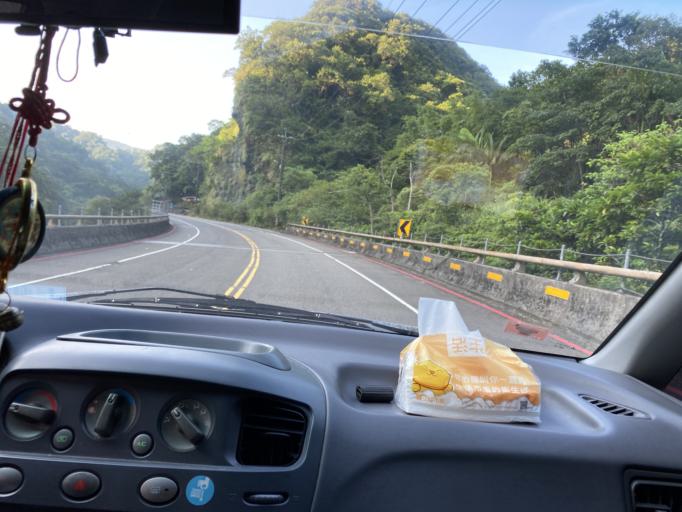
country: TW
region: Taiwan
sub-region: Keelung
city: Keelung
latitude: 25.0372
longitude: 121.7792
